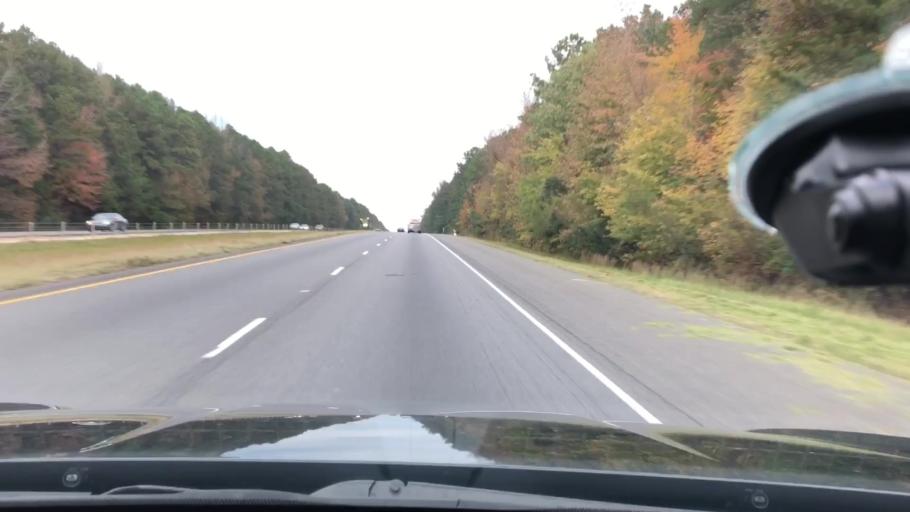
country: US
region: Arkansas
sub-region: Clark County
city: Arkadelphia
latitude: 34.2708
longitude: -92.9708
